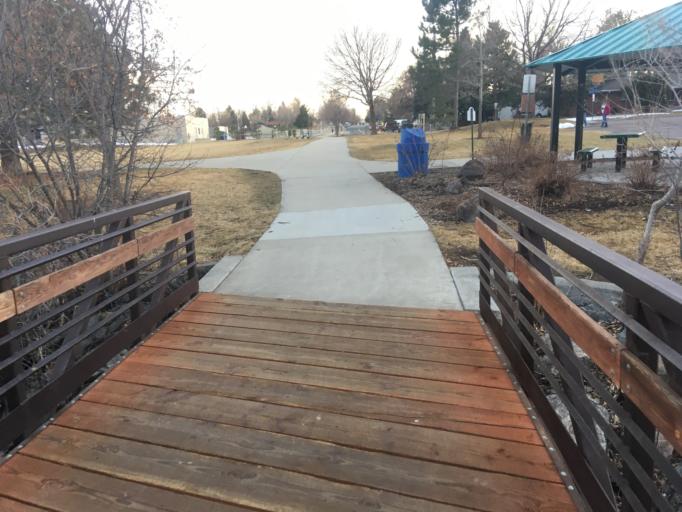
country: US
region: Colorado
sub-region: Broomfield County
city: Broomfield
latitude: 39.9221
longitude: -105.0796
